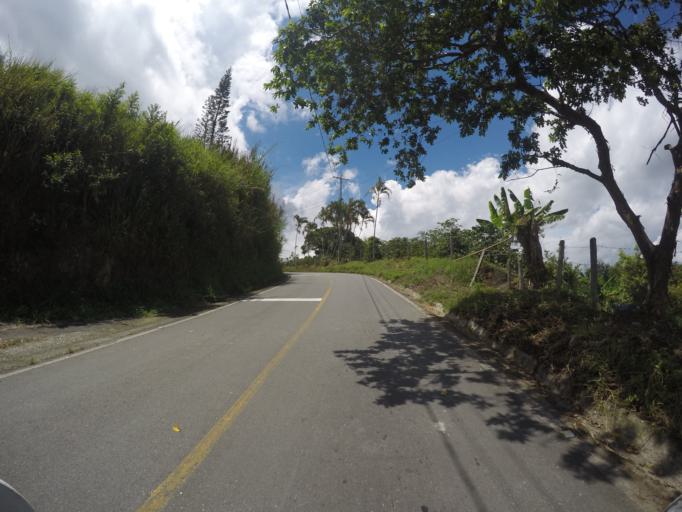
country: CO
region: Quindio
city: Quimbaya
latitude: 4.6298
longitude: -75.7172
